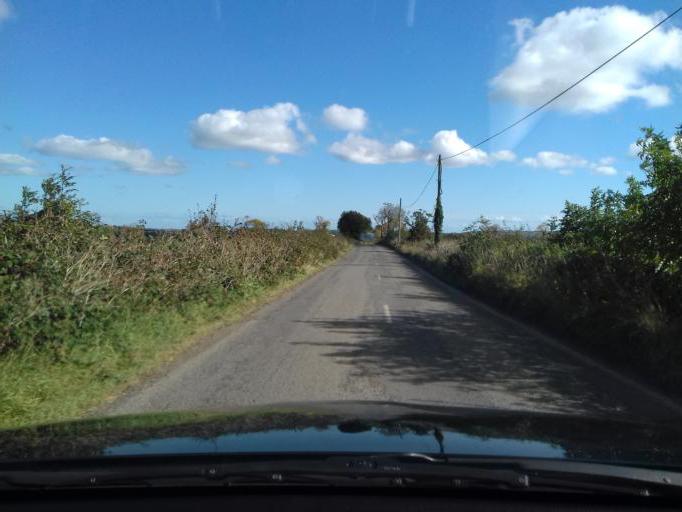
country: IE
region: Leinster
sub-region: An Mhi
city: Slane
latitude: 53.6868
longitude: -6.5279
